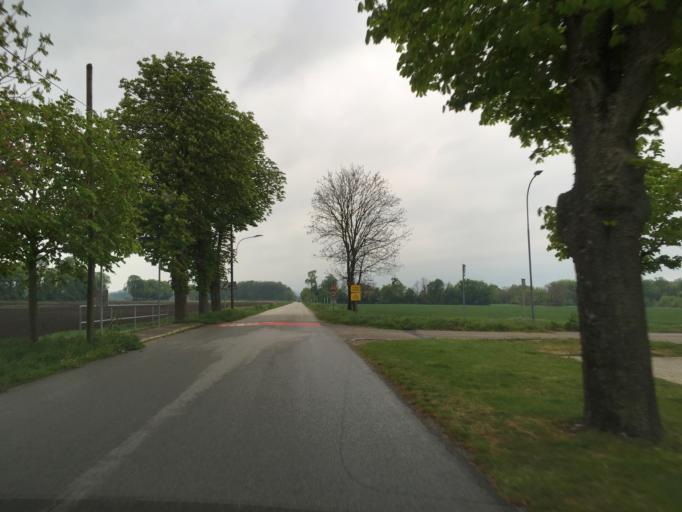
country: AT
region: Lower Austria
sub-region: Politischer Bezirk Bruck an der Leitha
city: Bruck an der Leitha
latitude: 48.0140
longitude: 16.7714
